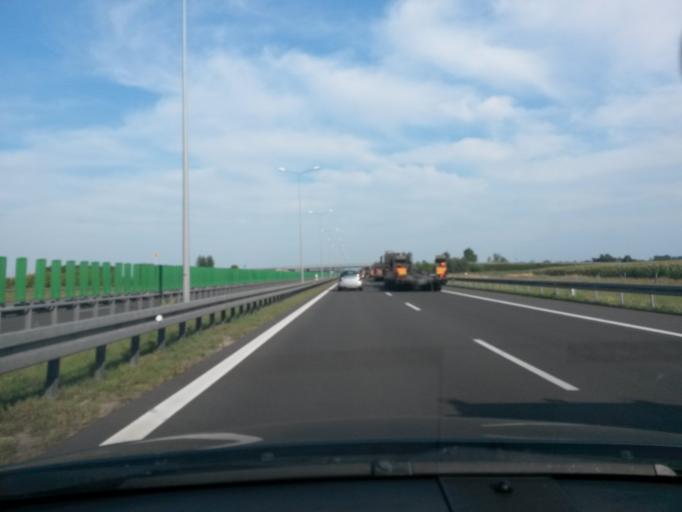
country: PL
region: Greater Poland Voivodeship
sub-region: Powiat slupecki
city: Strzalkowo
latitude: 52.2539
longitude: 17.8203
